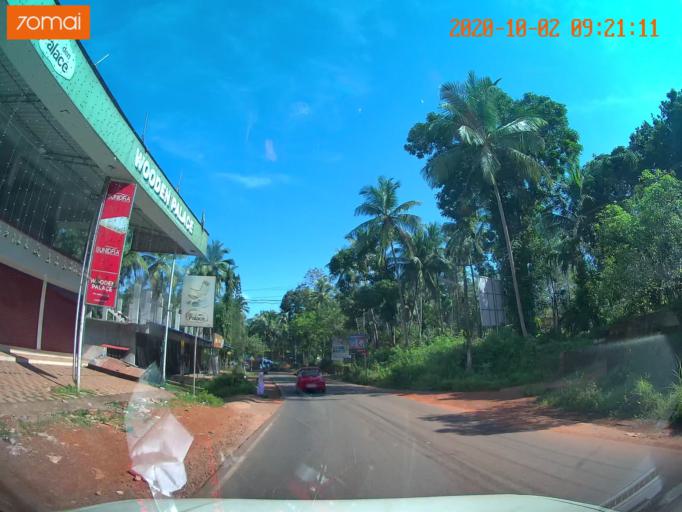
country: IN
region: Kerala
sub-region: Kozhikode
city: Naduvannur
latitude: 11.5720
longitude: 75.7538
